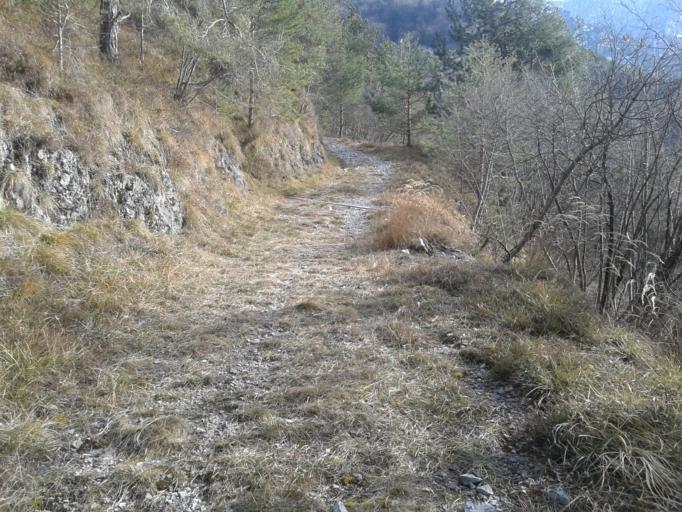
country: IT
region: Trentino-Alto Adige
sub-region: Provincia di Trento
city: Storo
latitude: 45.8367
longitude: 10.5711
